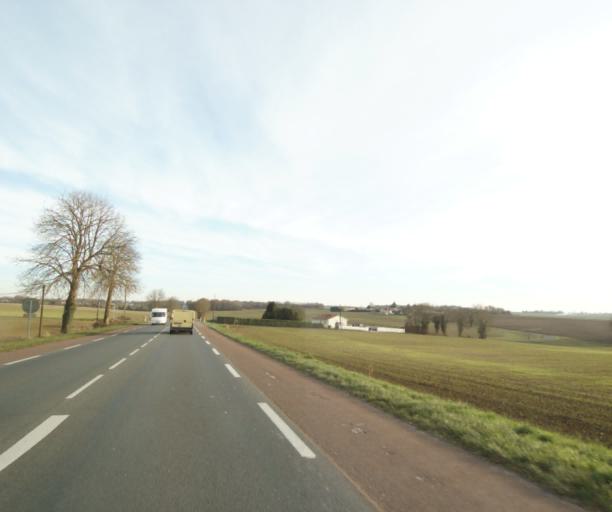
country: FR
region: Poitou-Charentes
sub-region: Departement de la Charente-Maritime
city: Saint-Georges-des-Coteaux
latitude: 45.7854
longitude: -0.7153
